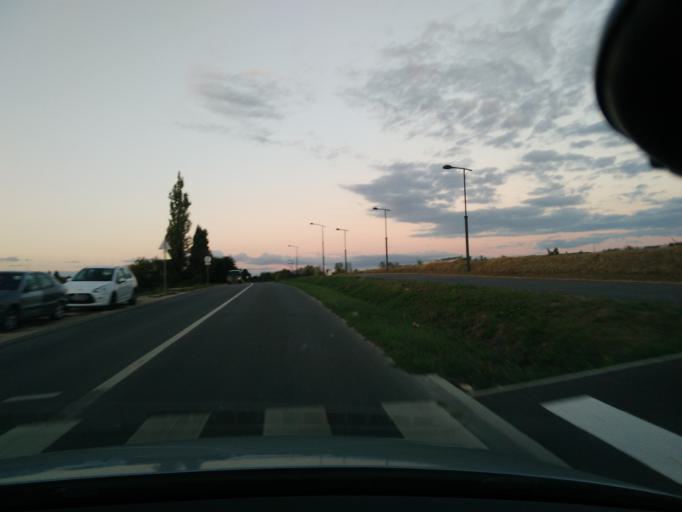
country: FR
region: Ile-de-France
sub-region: Departement de Seine-et-Marne
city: Villenoy
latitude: 48.9346
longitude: 2.8670
